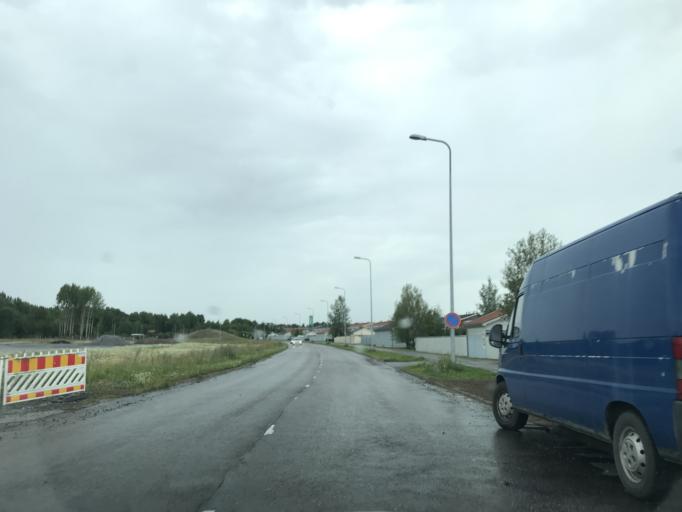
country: FI
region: Uusimaa
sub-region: Helsinki
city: Vihti
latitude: 60.3244
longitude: 24.3160
